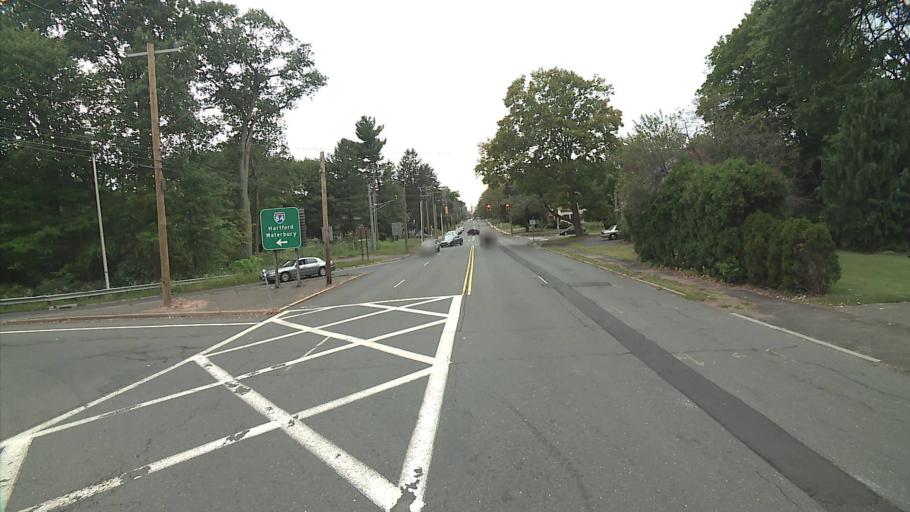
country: US
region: Connecticut
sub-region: Hartford County
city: West Hartford
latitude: 41.7543
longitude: -72.7370
